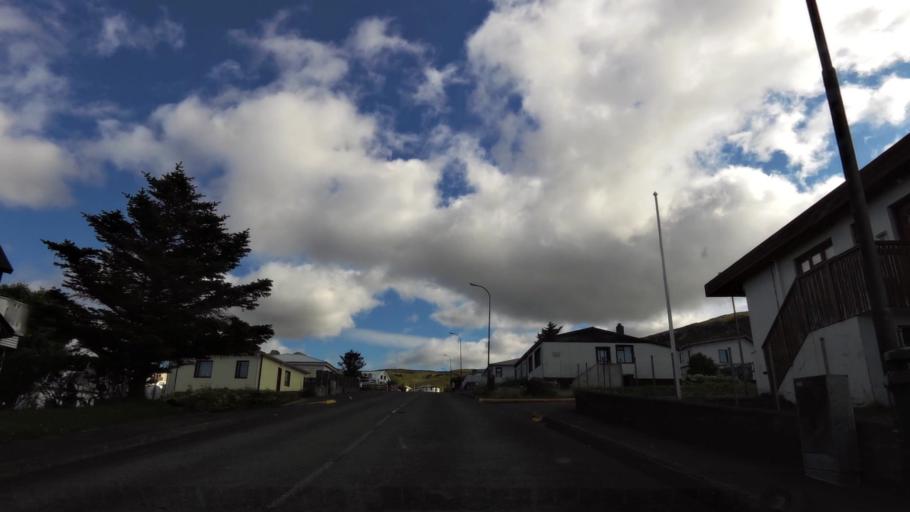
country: IS
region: West
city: Olafsvik
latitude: 64.8942
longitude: -23.7100
